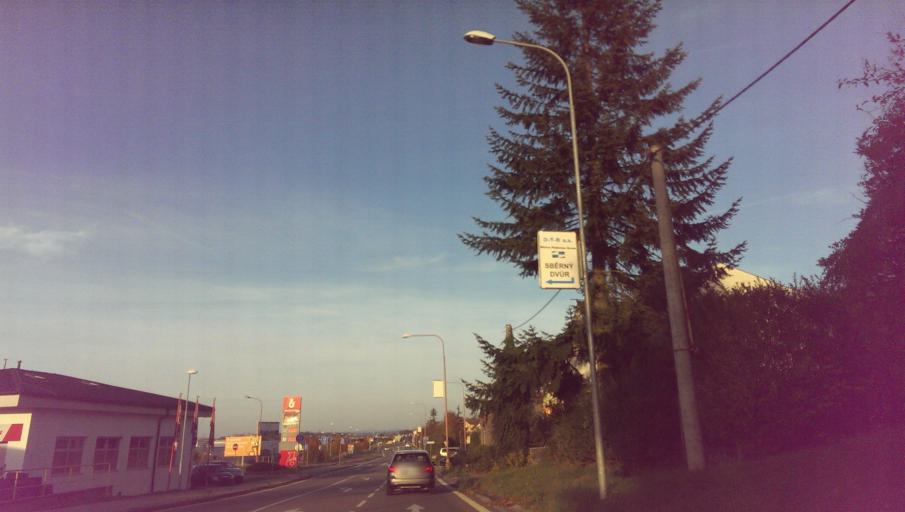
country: CZ
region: Zlin
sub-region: Okres Uherske Hradiste
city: Uherske Hradiste
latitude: 49.0759
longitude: 17.4832
